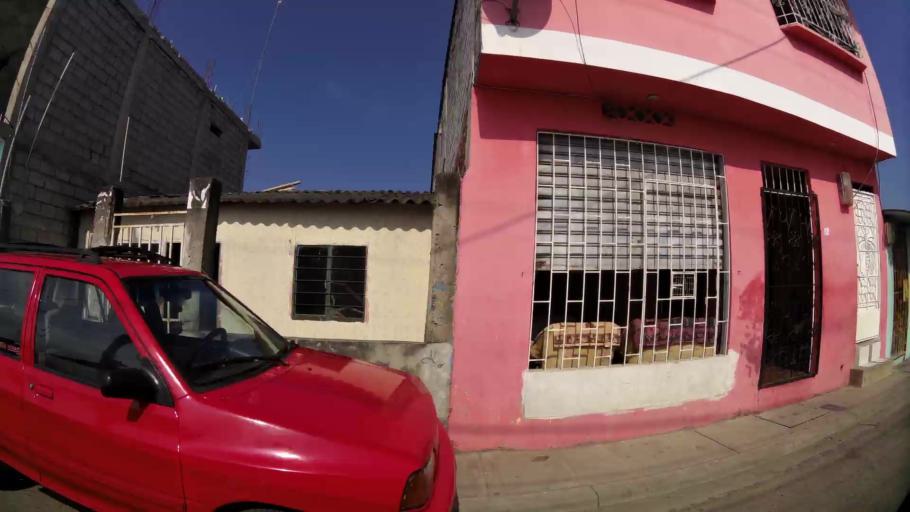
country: EC
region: Guayas
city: Eloy Alfaro
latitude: -2.1626
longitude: -79.7891
